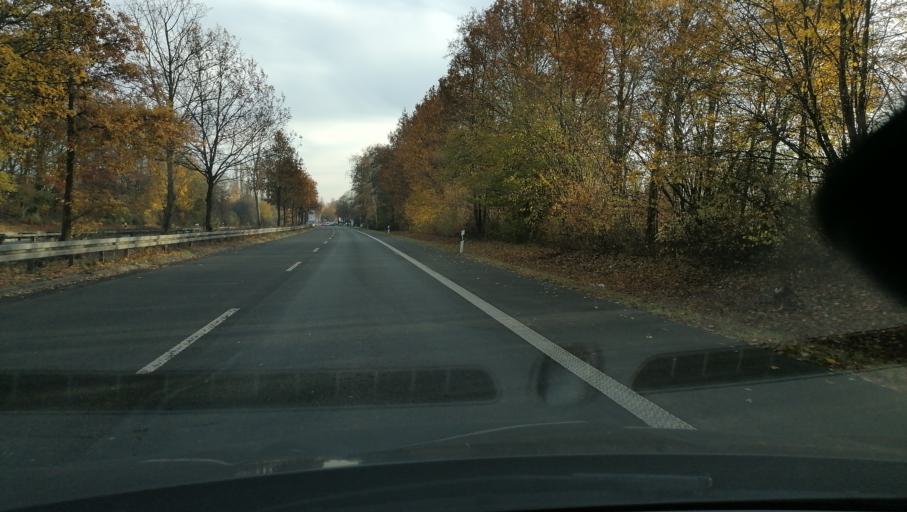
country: DE
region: North Rhine-Westphalia
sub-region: Regierungsbezirk Arnsberg
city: Dortmund
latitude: 51.5448
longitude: 7.4051
